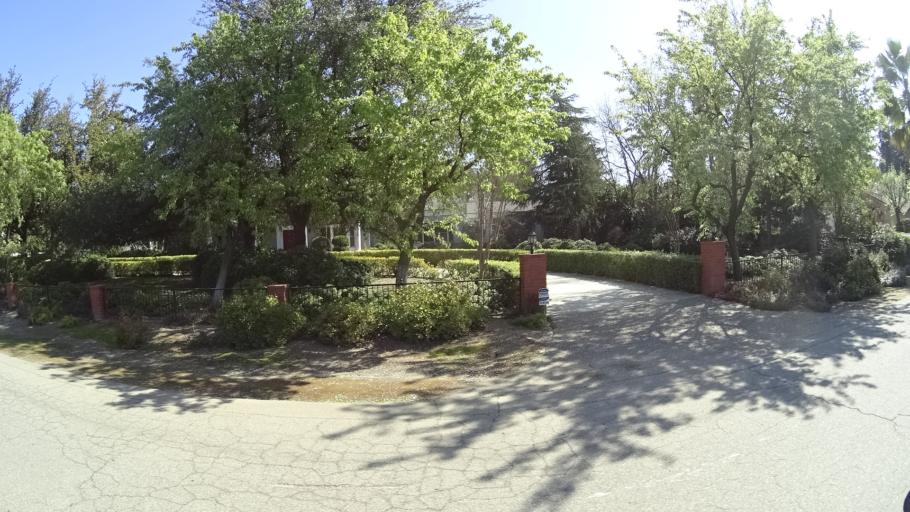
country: US
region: California
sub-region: Fresno County
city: Fresno
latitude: 36.8460
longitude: -119.8245
